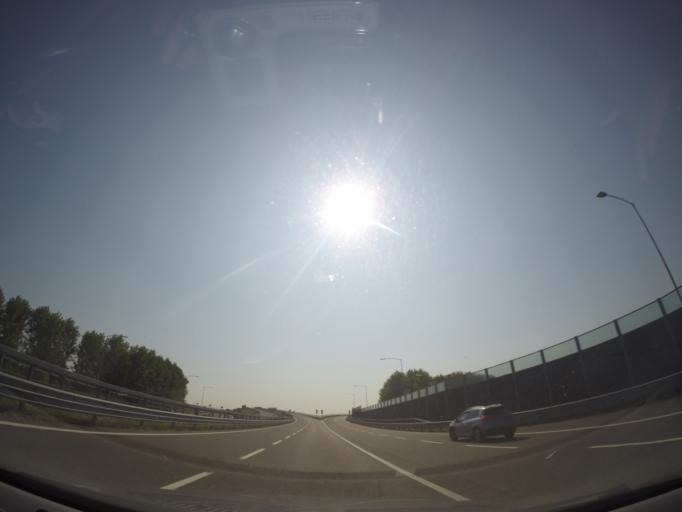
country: IT
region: Lombardy
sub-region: Citta metropolitana di Milano
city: Liscate
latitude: 45.4657
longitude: 9.4292
